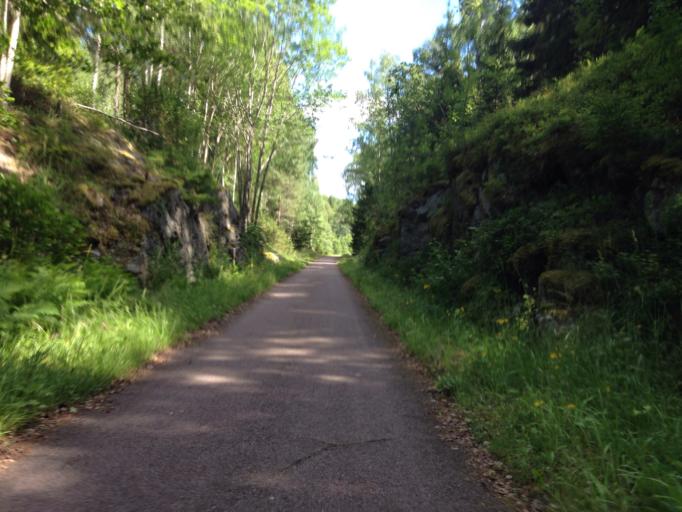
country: SE
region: Dalarna
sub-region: Ludvika Kommun
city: Grangesberg
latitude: 60.2148
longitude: 15.0423
